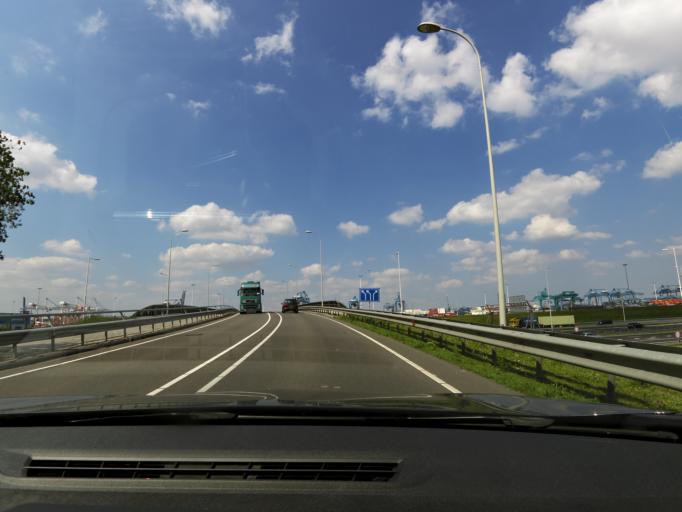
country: NL
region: South Holland
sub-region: Gemeente Albrandswaard
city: Rhoon
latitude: 51.8723
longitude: 4.4119
